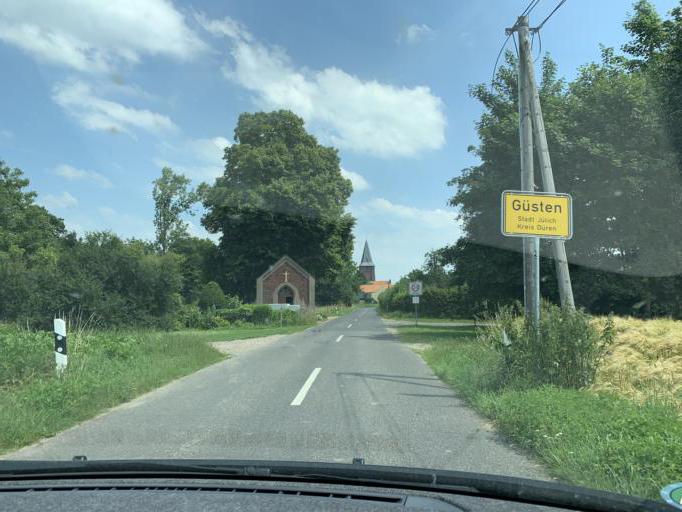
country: DE
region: North Rhine-Westphalia
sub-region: Regierungsbezirk Koln
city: Titz
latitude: 50.9593
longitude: 6.4261
